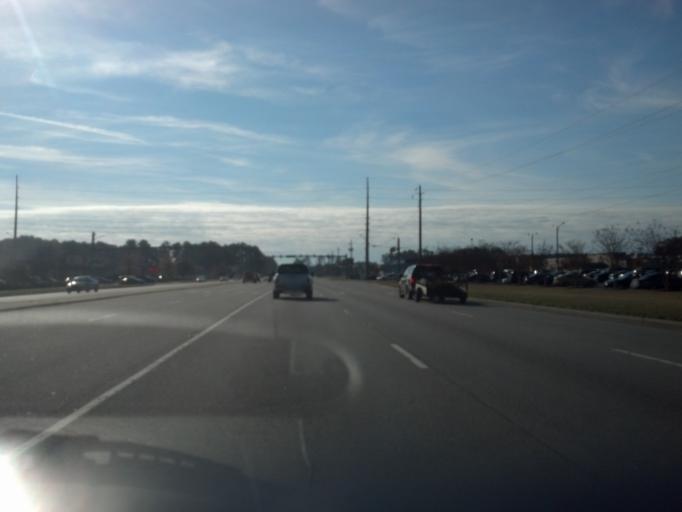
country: US
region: North Carolina
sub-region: Pitt County
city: Summerfield
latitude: 35.5495
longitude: -77.4056
